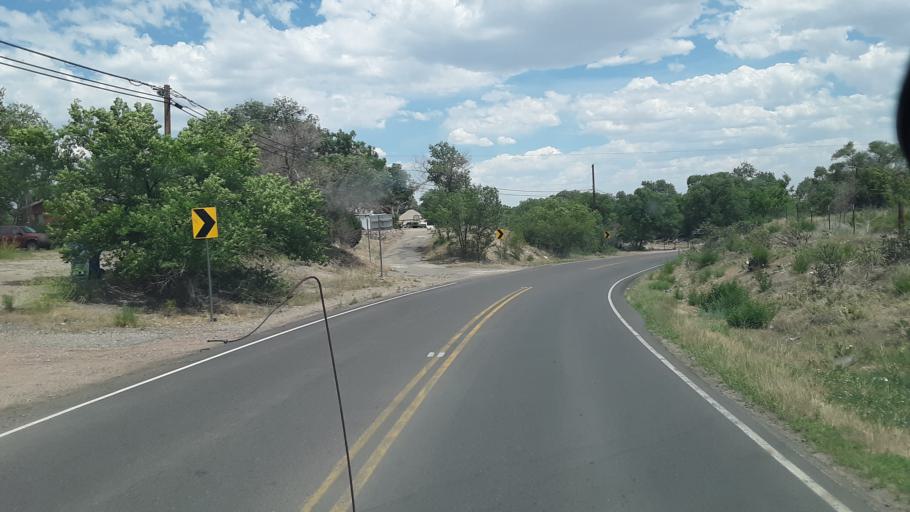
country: US
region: Colorado
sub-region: Fremont County
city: Lincoln Park
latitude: 38.4176
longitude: -105.1846
